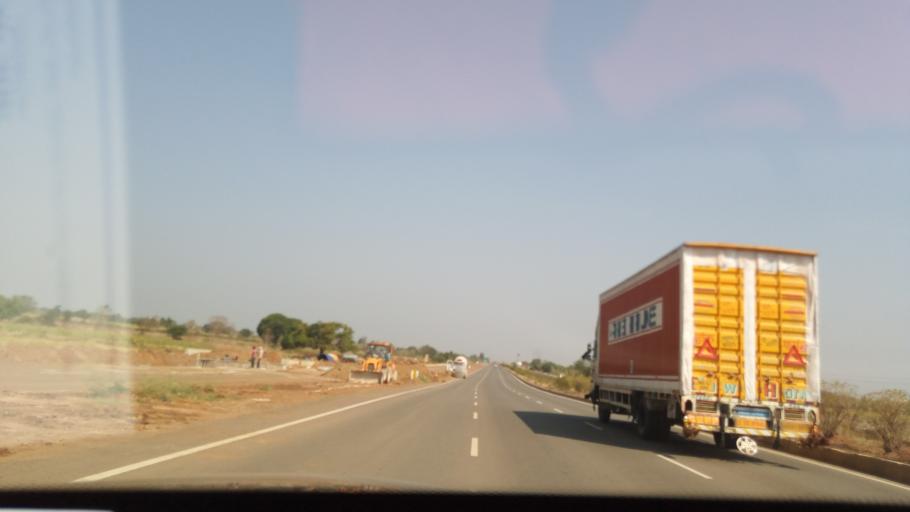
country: IN
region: Karnataka
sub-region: Dharwad
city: Kundgol
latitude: 15.1394
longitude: 75.1460
